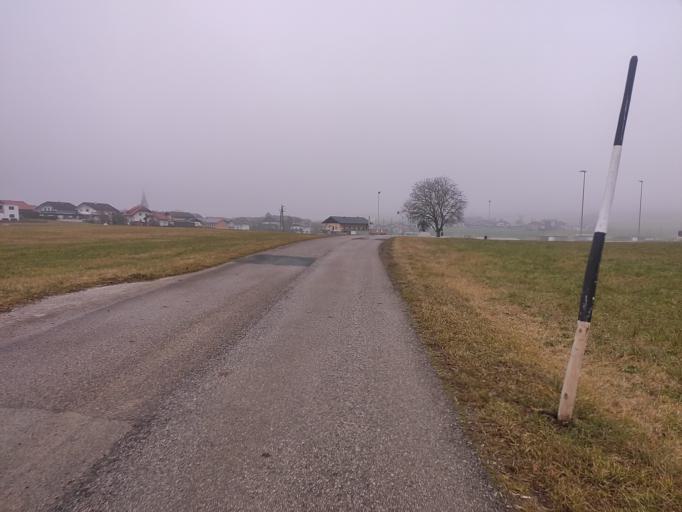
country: AT
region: Salzburg
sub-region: Politischer Bezirk Salzburg-Umgebung
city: Schleedorf
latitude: 47.9512
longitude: 13.1584
